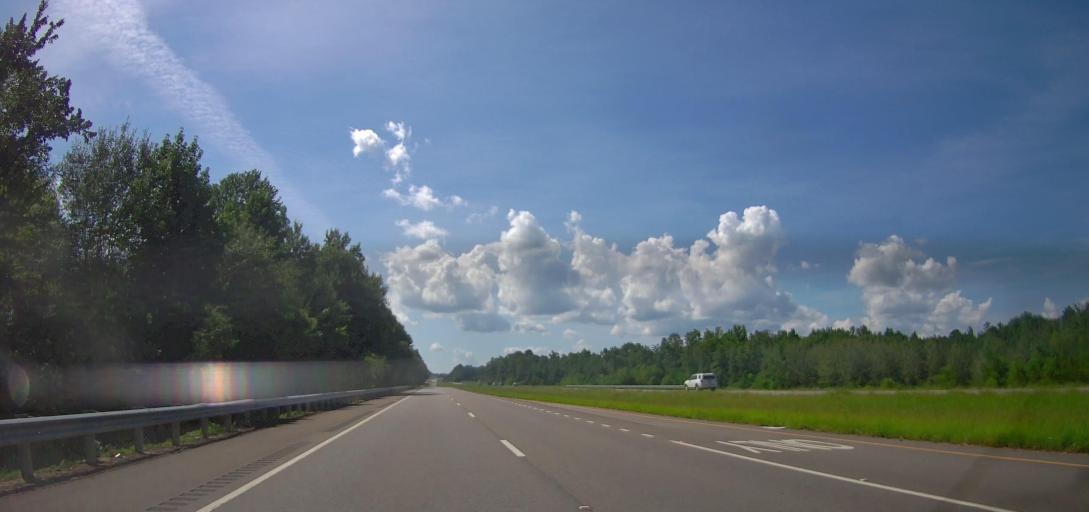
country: US
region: Alabama
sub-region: Pickens County
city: Gordo
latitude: 33.3449
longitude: -87.9474
